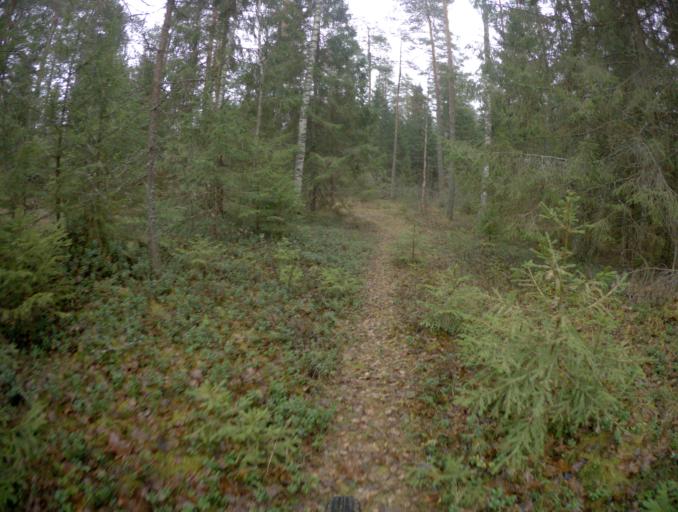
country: RU
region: Vladimir
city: Golovino
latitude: 56.0144
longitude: 40.4983
